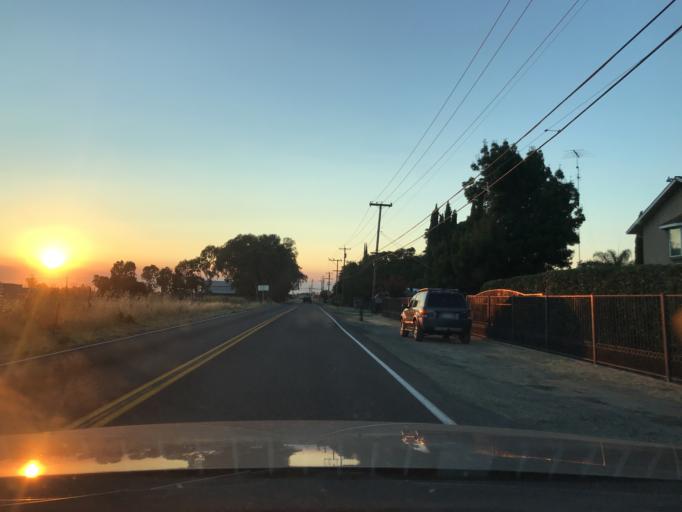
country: US
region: California
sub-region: Merced County
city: Merced
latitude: 37.3391
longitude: -120.5084
